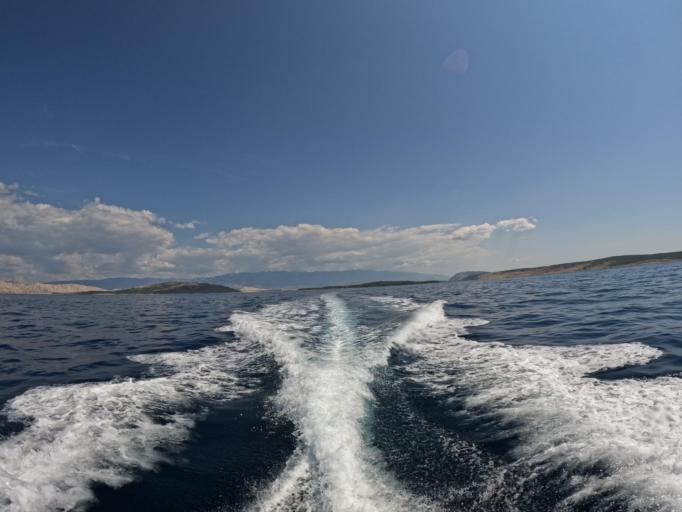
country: HR
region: Primorsko-Goranska
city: Lopar
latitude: 44.8645
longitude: 14.6869
